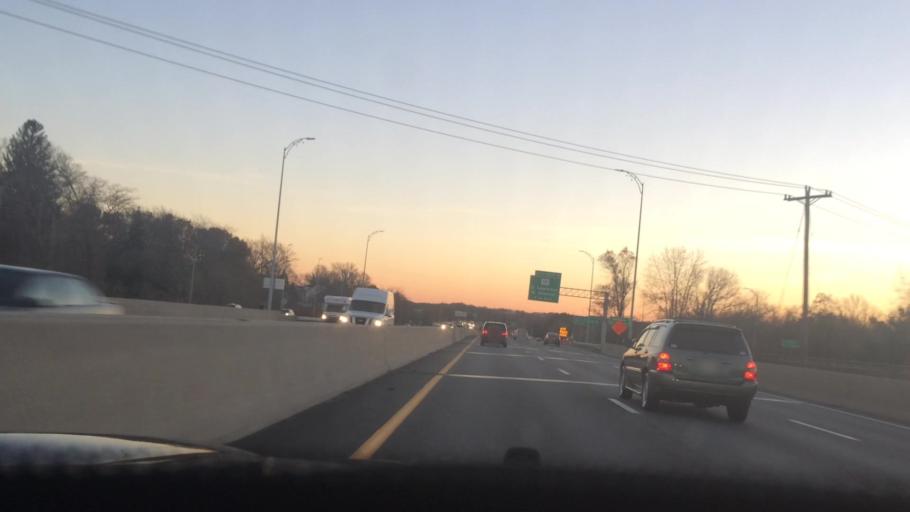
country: US
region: Massachusetts
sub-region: Essex County
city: North Andover
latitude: 42.7035
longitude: -71.1399
